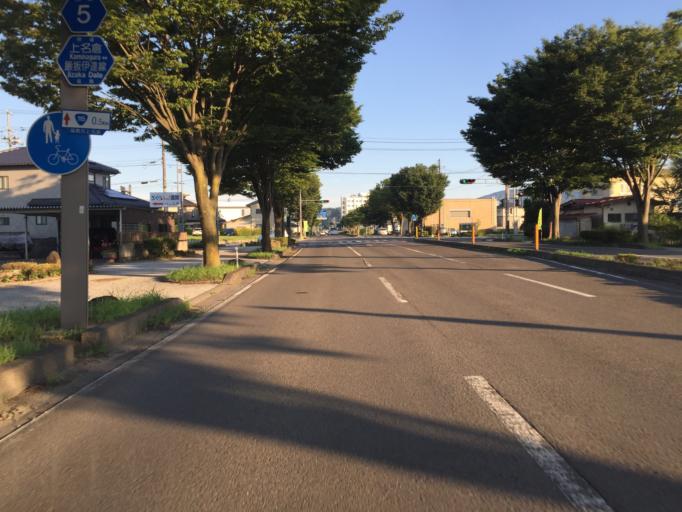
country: JP
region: Fukushima
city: Fukushima-shi
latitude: 37.7305
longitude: 140.3867
